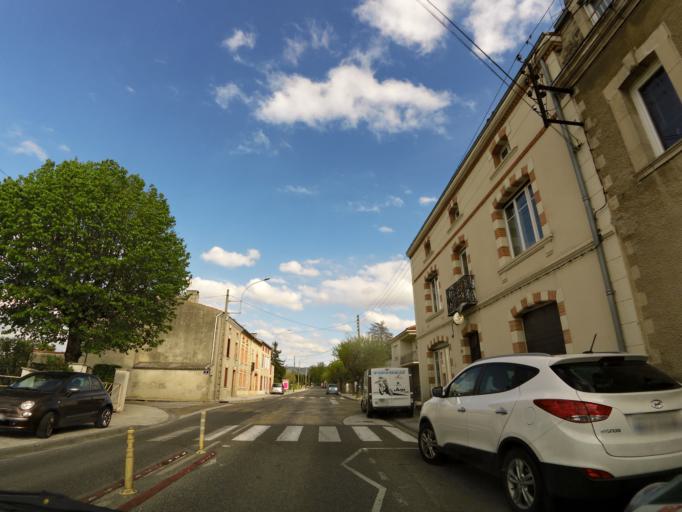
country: FR
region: Midi-Pyrenees
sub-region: Departement de la Haute-Garonne
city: Revel
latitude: 43.4573
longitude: 2.0093
